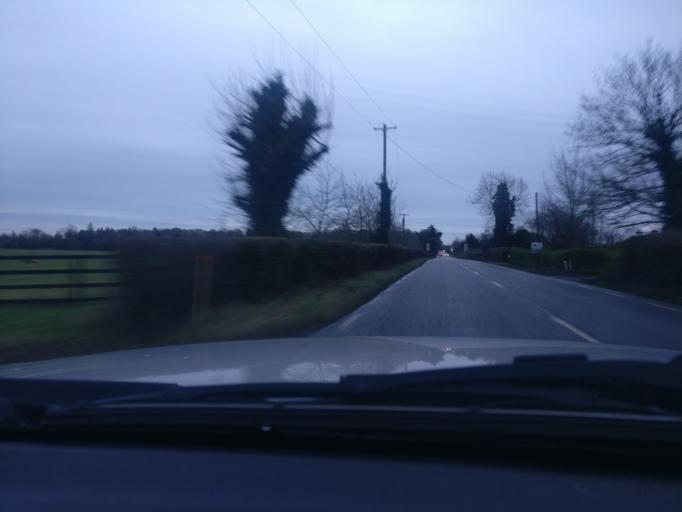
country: IE
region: Leinster
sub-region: An Mhi
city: Navan
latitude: 53.6748
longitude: -6.7443
